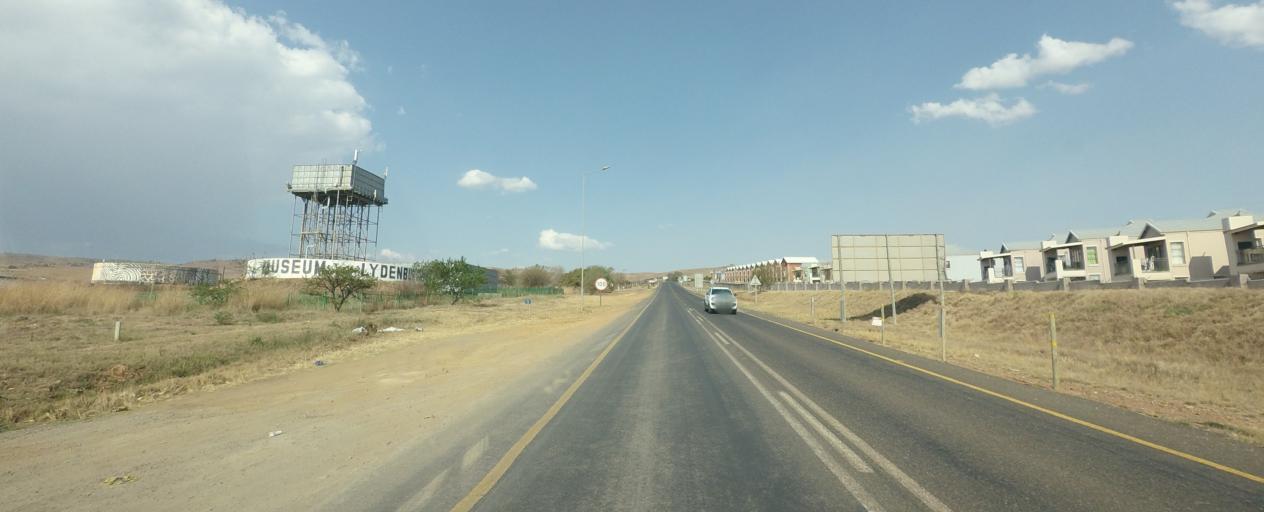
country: ZA
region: Mpumalanga
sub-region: Ehlanzeni District
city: Lydenburg
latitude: -25.1042
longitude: 30.4839
